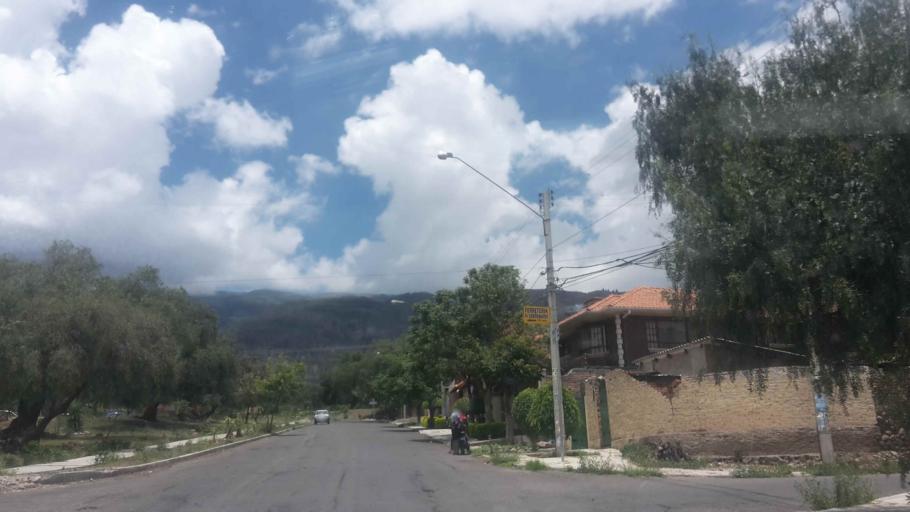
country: BO
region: Cochabamba
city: Cochabamba
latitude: -17.3637
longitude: -66.1560
